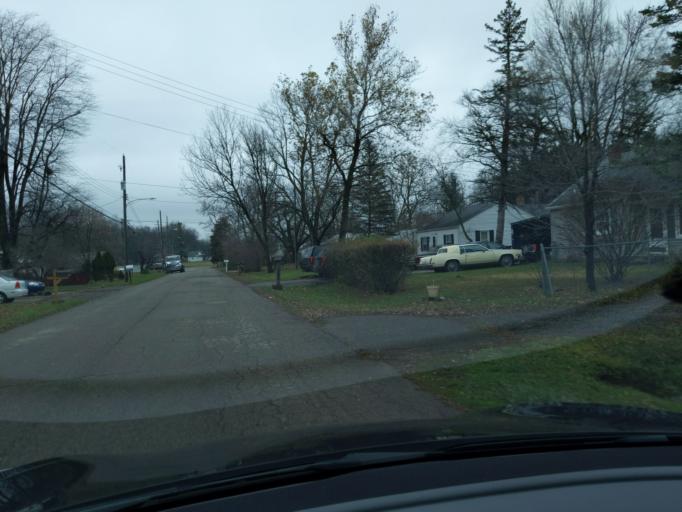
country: US
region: Michigan
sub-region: Ingham County
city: Lansing
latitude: 42.6813
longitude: -84.5714
